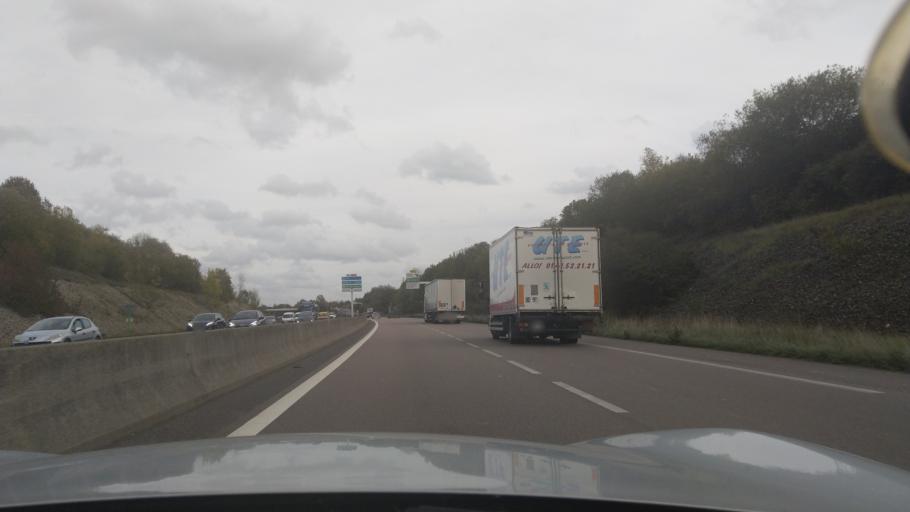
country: FR
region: Ile-de-France
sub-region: Departement du Val-d'Oise
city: Louvres
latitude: 49.0321
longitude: 2.4919
